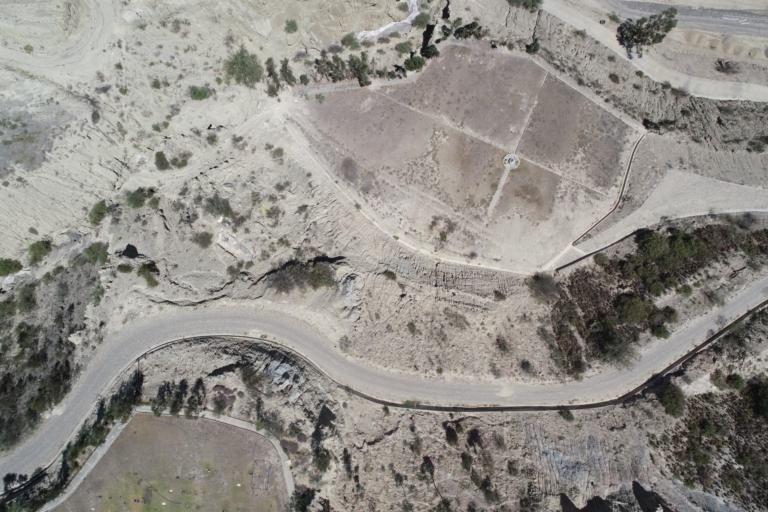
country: BO
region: La Paz
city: La Paz
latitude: -16.6187
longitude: -68.0594
